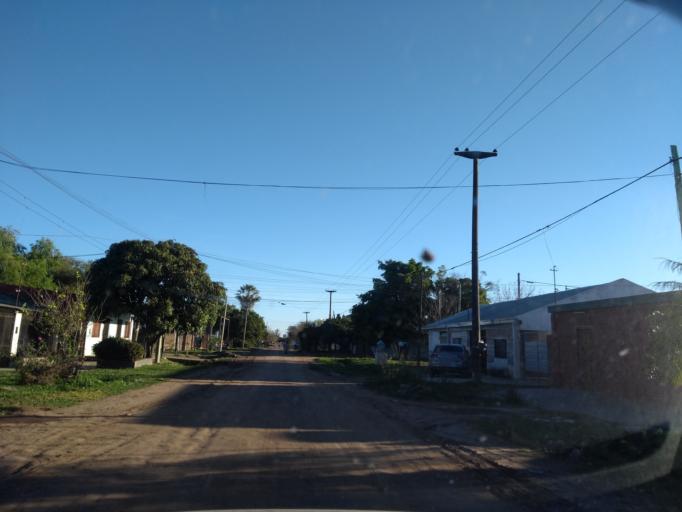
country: AR
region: Chaco
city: Barranqueras
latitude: -27.4896
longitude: -58.9349
